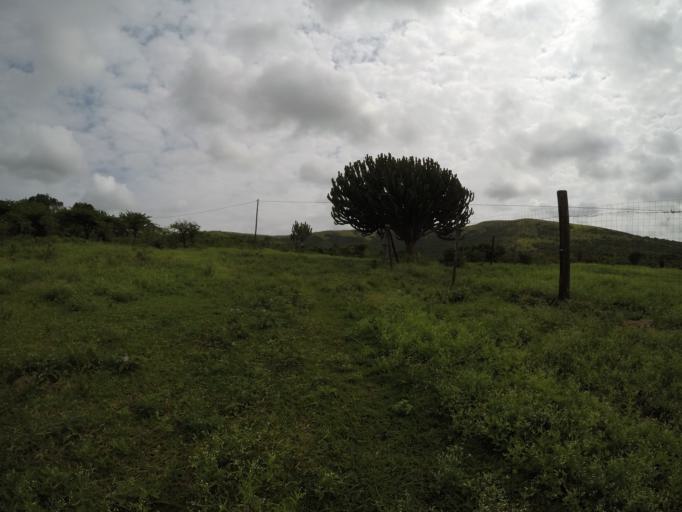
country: ZA
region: KwaZulu-Natal
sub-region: uThungulu District Municipality
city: Empangeni
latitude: -28.6129
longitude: 31.9018
